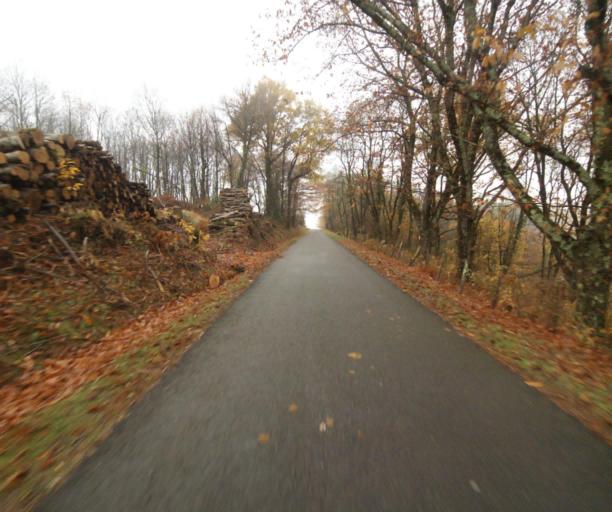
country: FR
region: Limousin
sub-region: Departement de la Correze
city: Cornil
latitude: 45.2000
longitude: 1.6405
